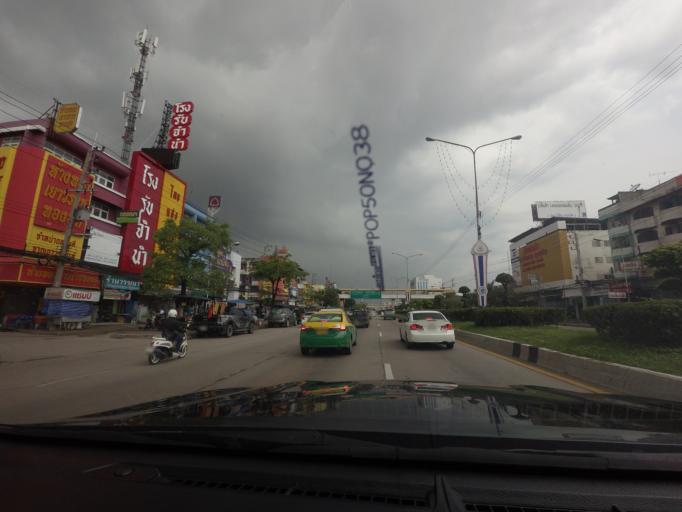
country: TH
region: Bangkok
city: Nong Khaem
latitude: 13.7046
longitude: 100.3167
